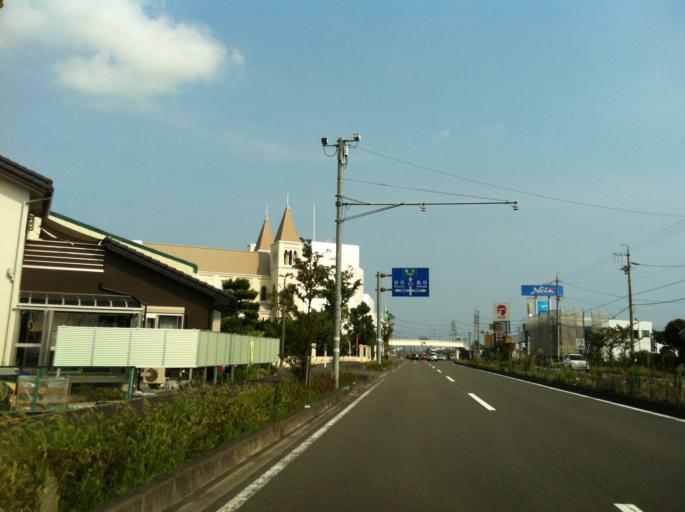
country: JP
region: Shizuoka
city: Fujieda
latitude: 34.8952
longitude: 138.2805
